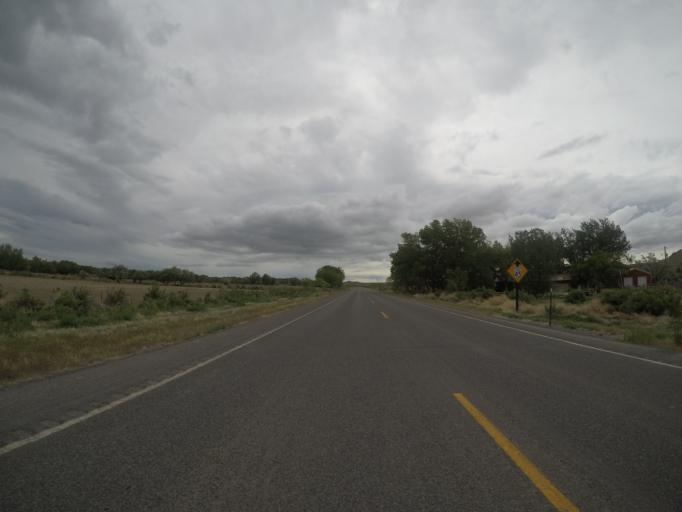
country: US
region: Wyoming
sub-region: Big Horn County
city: Lovell
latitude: 44.8680
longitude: -108.3247
